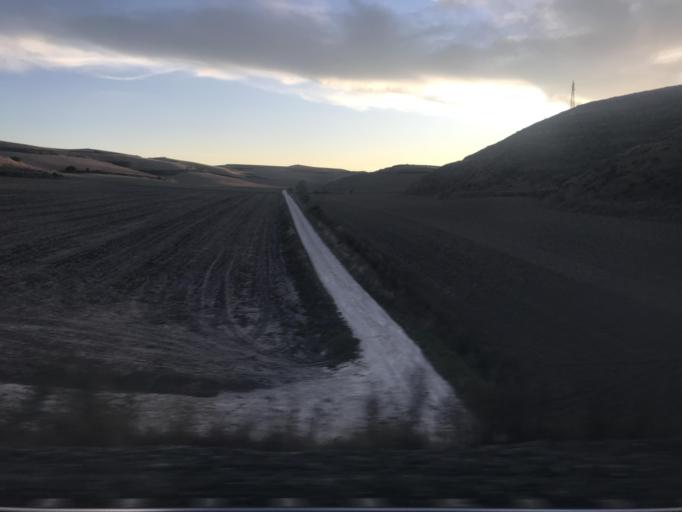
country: ES
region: Castille and Leon
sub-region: Provincia de Burgos
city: Santa Maria del Invierno
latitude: 42.4395
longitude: -3.4429
